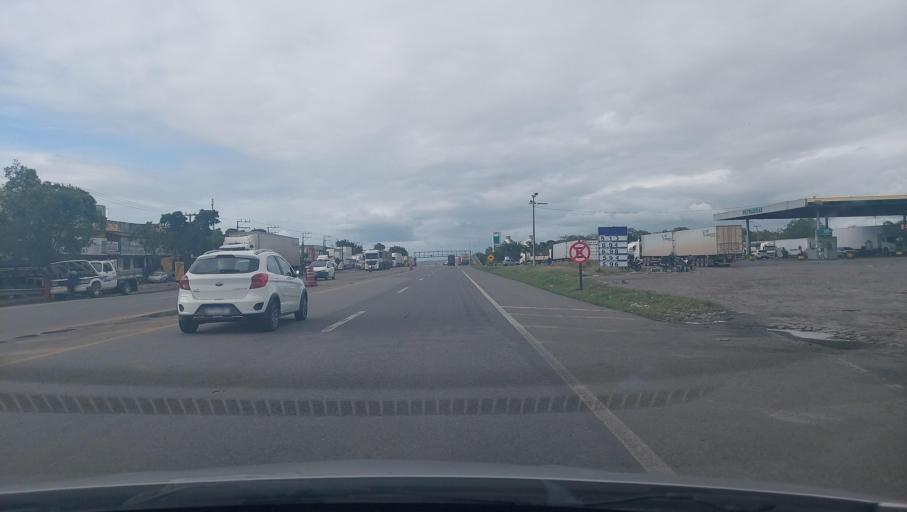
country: BR
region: Bahia
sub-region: Santo Estevao
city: Santo Estevao
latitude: -12.4408
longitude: -39.2293
